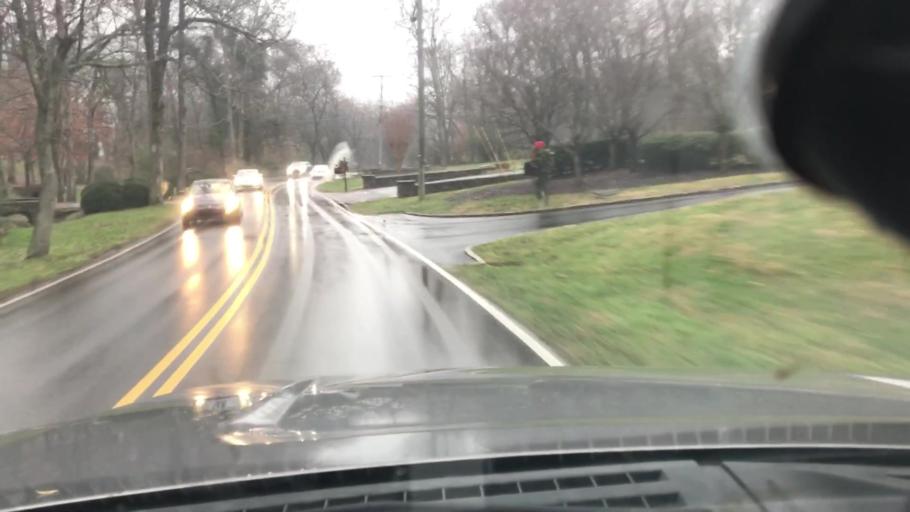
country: US
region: Tennessee
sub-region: Davidson County
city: Forest Hills
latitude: 36.0718
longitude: -86.8611
